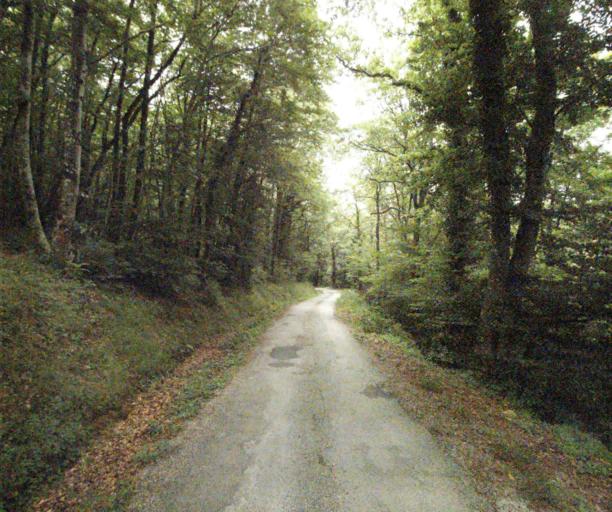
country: FR
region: Midi-Pyrenees
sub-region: Departement du Tarn
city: Soreze
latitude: 43.4313
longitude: 2.0900
